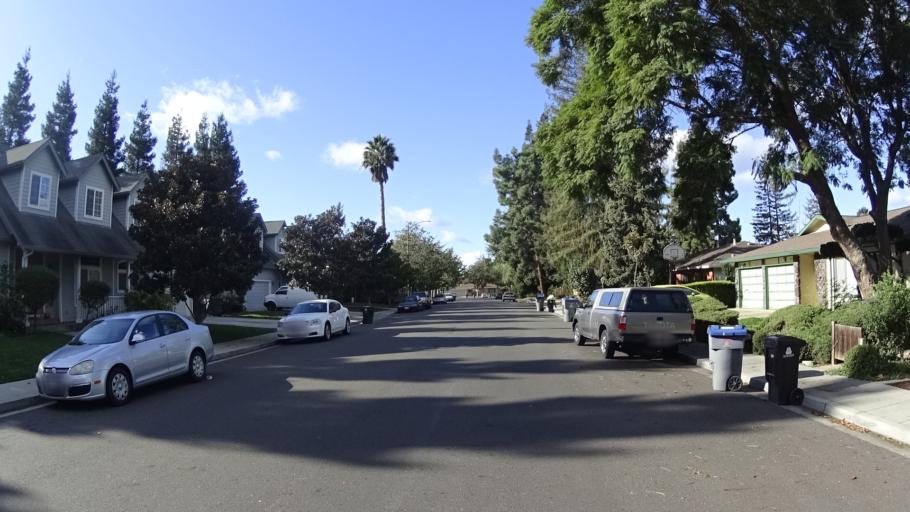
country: US
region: California
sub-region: Santa Clara County
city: Mountain View
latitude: 37.3775
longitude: -122.0612
